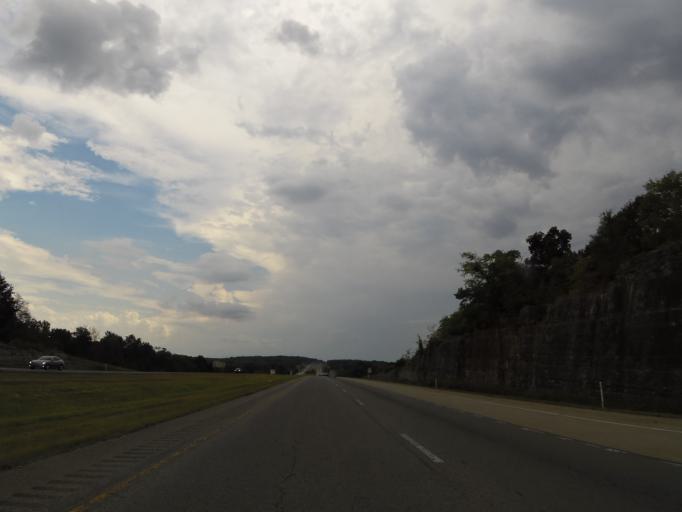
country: US
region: Tennessee
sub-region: Wilson County
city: Rural Hill
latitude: 36.0296
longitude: -86.4288
